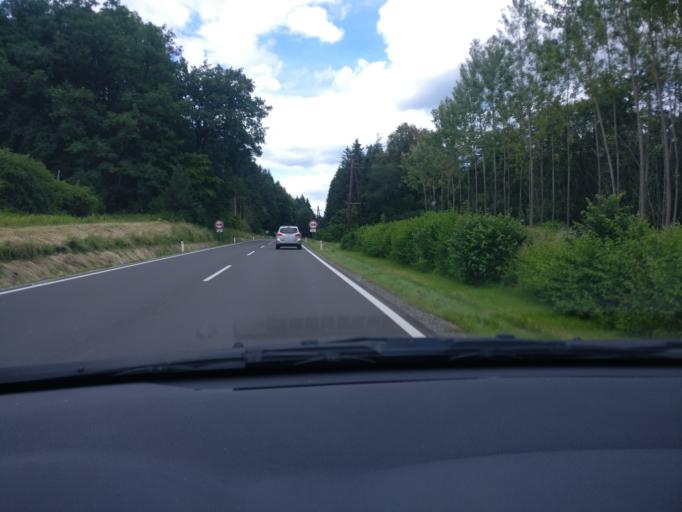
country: AT
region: Styria
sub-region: Politischer Bezirk Weiz
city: Oberrettenbach
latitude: 47.1547
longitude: 15.7712
